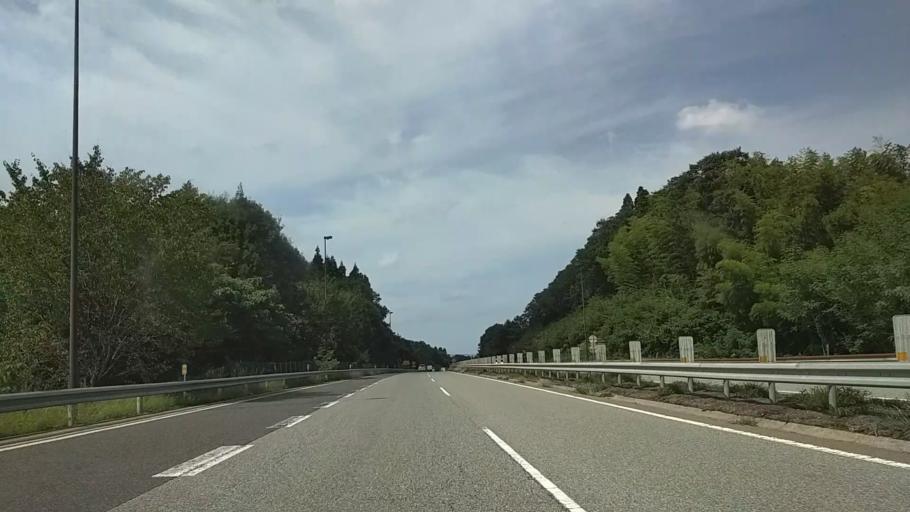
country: JP
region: Toyama
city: Kuragaki-kosugi
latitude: 36.6830
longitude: 137.1071
